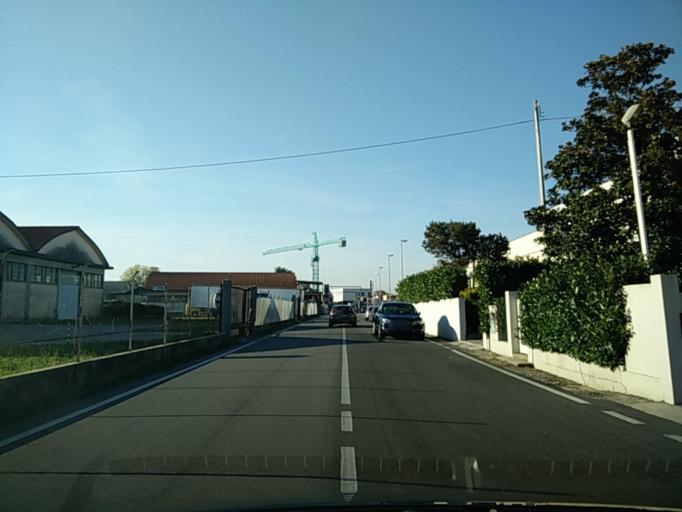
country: IT
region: Veneto
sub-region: Provincia di Treviso
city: Treviso
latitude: 45.6910
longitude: 12.2460
